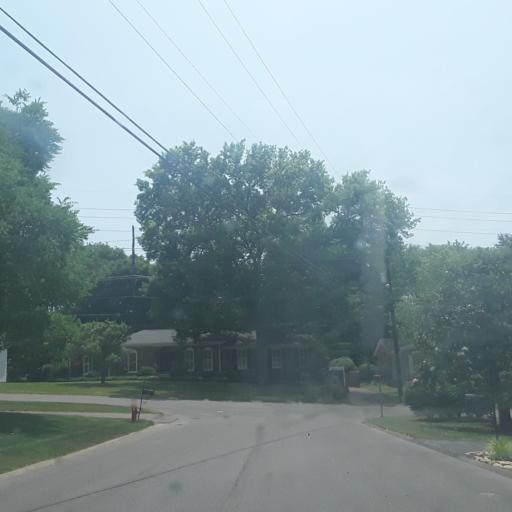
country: US
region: Tennessee
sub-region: Williamson County
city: Brentwood
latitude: 36.0553
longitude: -86.7580
